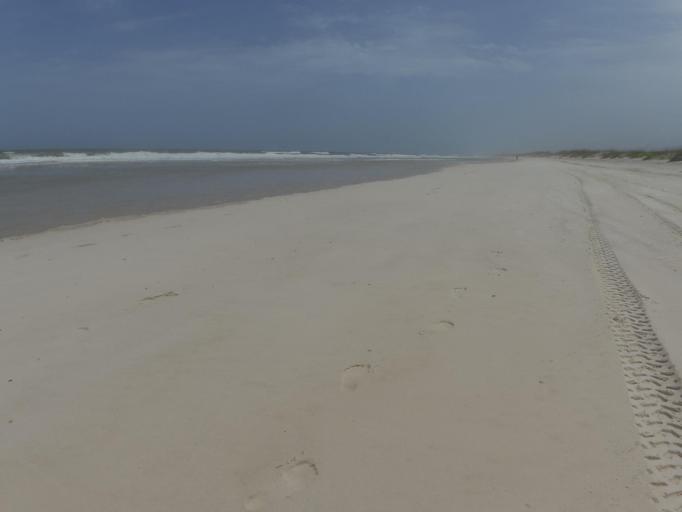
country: US
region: Florida
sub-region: Saint Johns County
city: Saint Augustine
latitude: 29.8950
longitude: -81.2759
